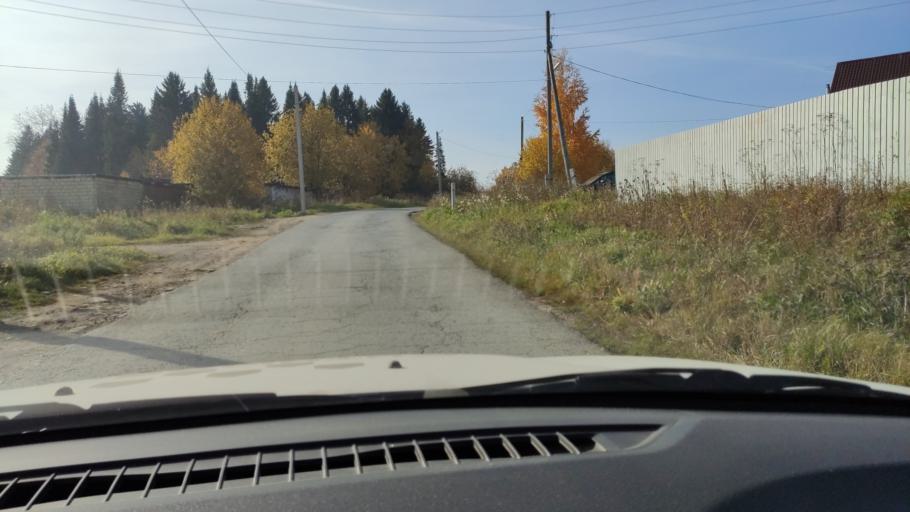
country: RU
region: Perm
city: Sylva
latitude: 58.0403
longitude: 56.7487
